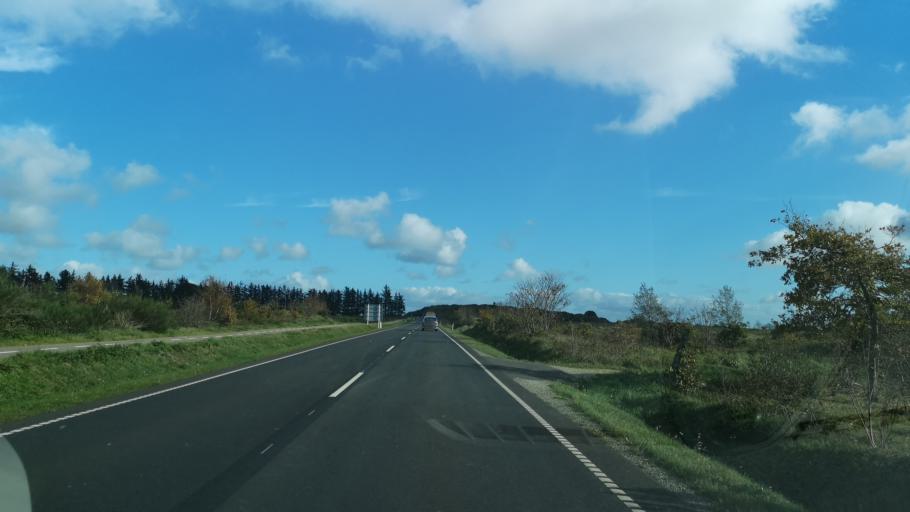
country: DK
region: South Denmark
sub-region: Varde Kommune
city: Oksbol
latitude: 55.7259
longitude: 8.2527
